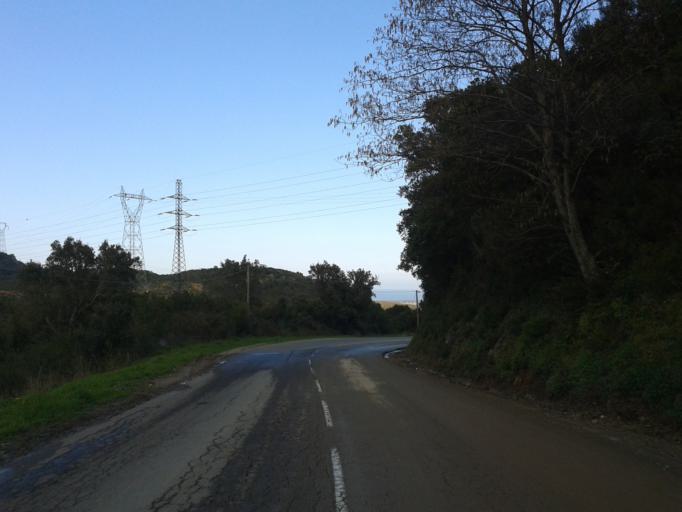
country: FR
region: Corsica
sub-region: Departement de la Haute-Corse
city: Biguglia
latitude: 42.5985
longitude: 9.4189
